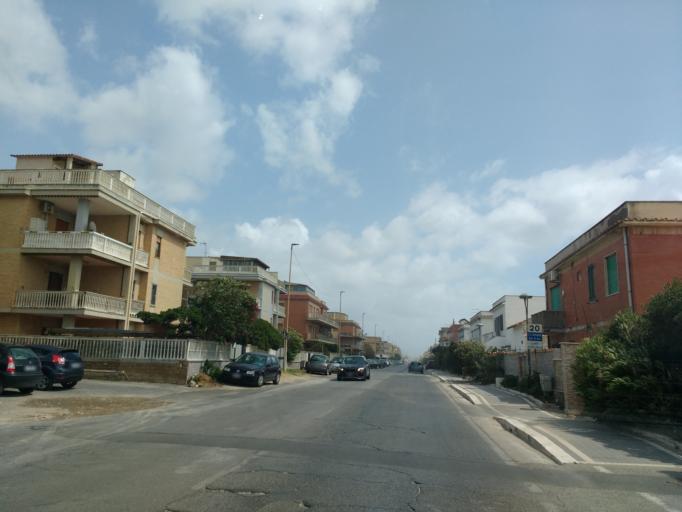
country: IT
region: Latium
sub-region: Citta metropolitana di Roma Capitale
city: Ardea
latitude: 41.5905
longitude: 12.4948
